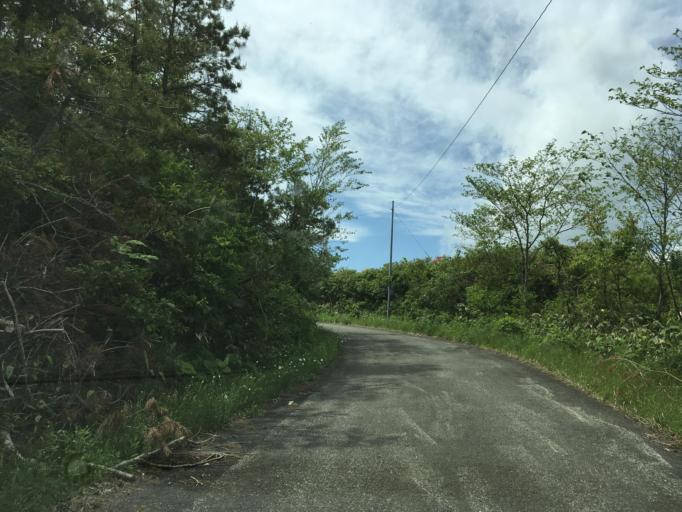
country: JP
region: Iwate
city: Mizusawa
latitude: 39.1320
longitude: 141.3156
